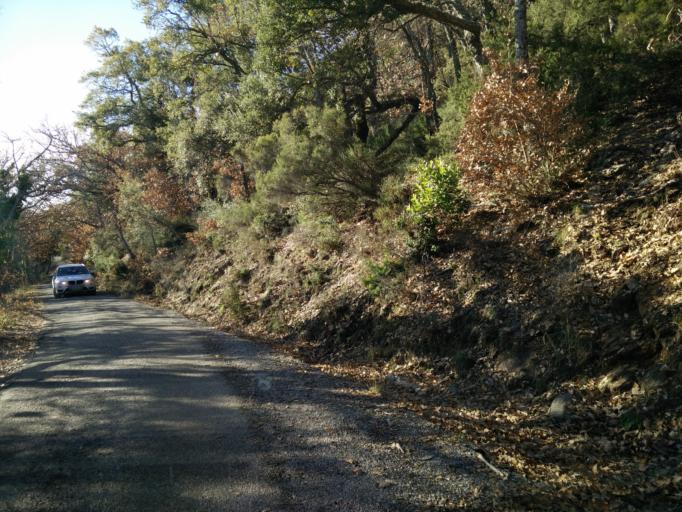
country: FR
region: Provence-Alpes-Cote d'Azur
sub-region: Departement du Var
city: Gonfaron
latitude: 43.2796
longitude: 6.2946
